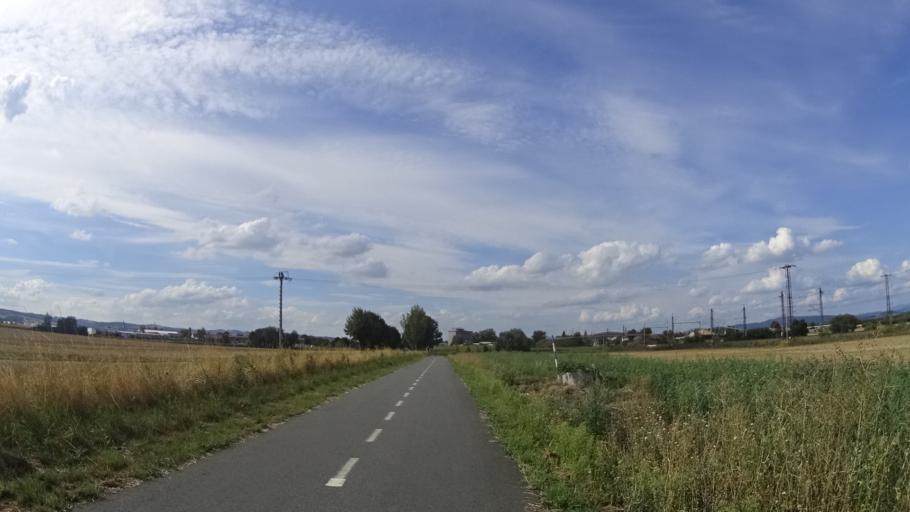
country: CZ
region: Olomoucky
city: Moravicany
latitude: 49.7669
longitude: 16.9478
